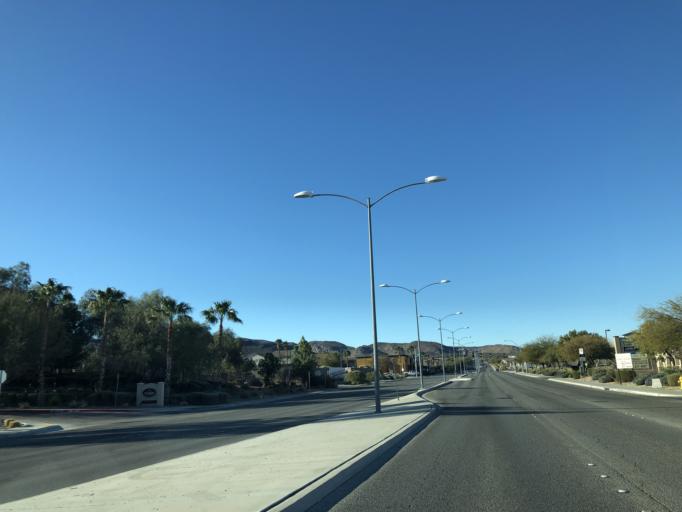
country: US
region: Nevada
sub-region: Clark County
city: Whitney
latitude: 36.0176
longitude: -115.0547
